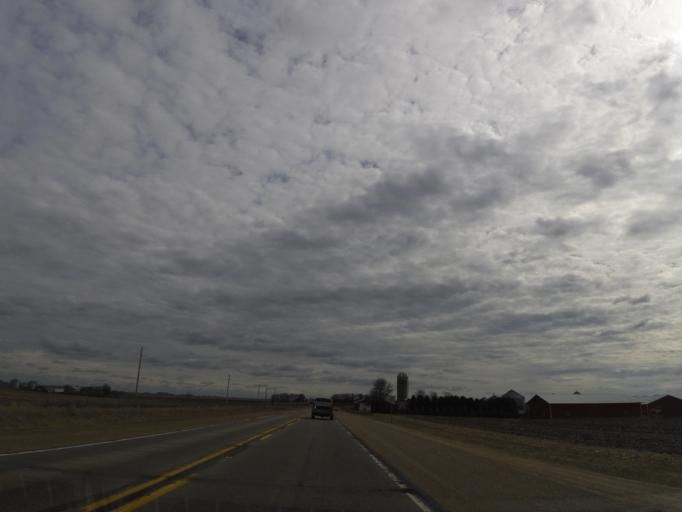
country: US
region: Iowa
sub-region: Howard County
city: Cresco
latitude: 43.3199
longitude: -92.2990
